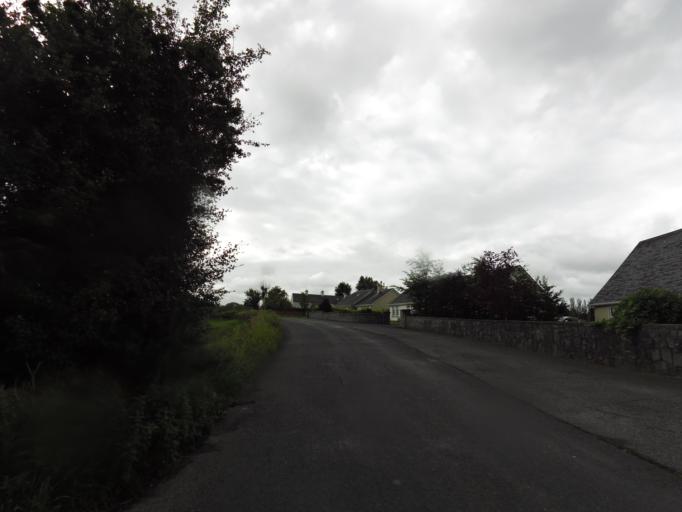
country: IE
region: Connaught
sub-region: County Galway
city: Athenry
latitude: 53.2878
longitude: -8.6927
